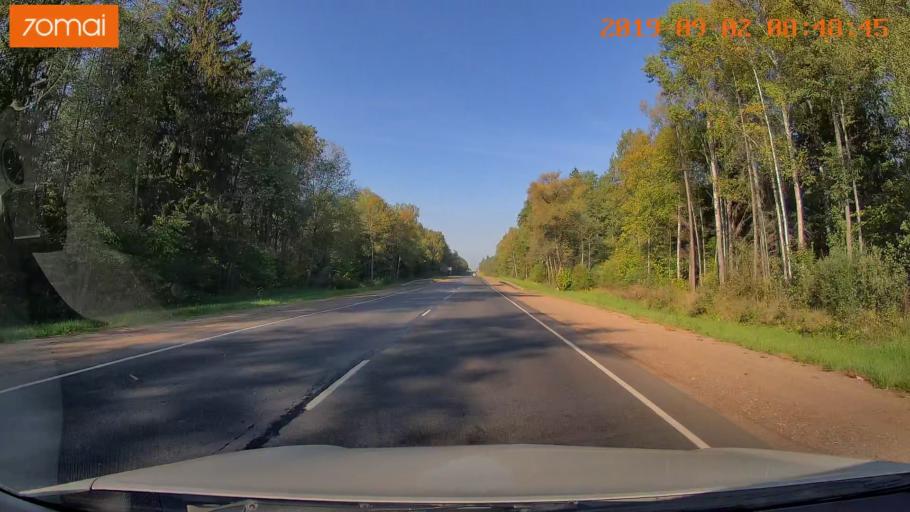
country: RU
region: Kaluga
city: Medyn'
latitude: 54.9667
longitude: 35.9243
